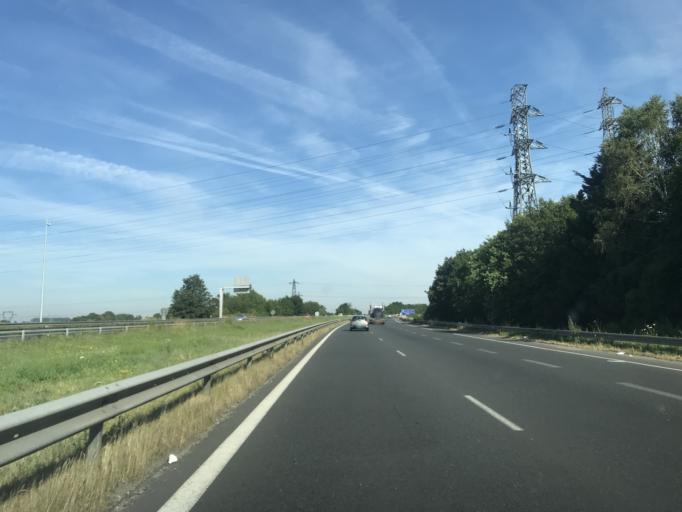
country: FR
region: Haute-Normandie
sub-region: Departement de la Seine-Maritime
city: La Vaupaliere
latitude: 49.4819
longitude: 1.0086
